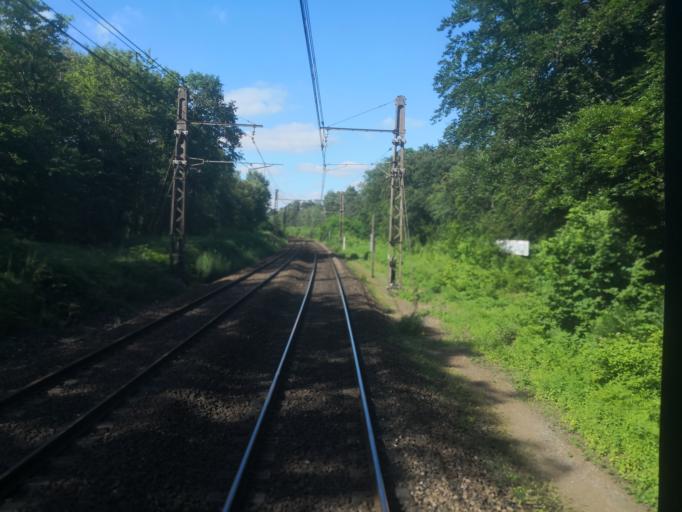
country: FR
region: Ile-de-France
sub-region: Departement de Seine-et-Marne
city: Samoreau
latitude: 48.4259
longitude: 2.7353
